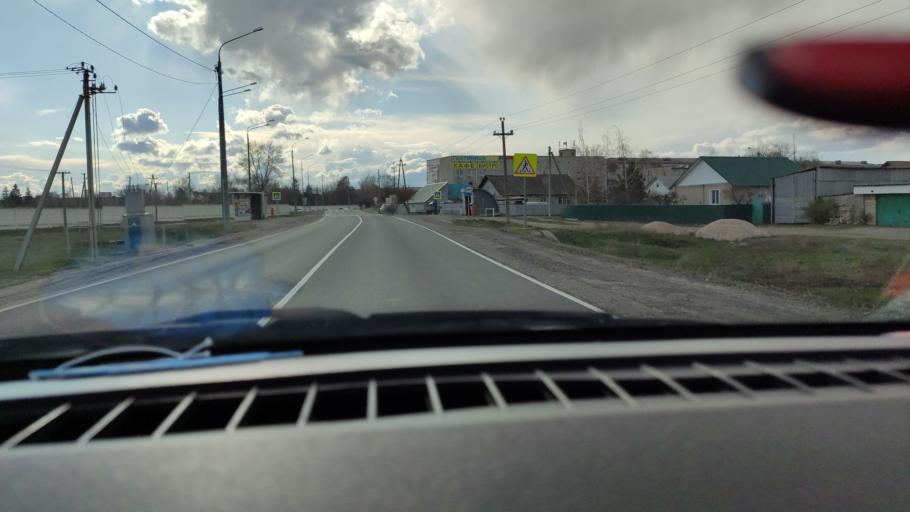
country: RU
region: Saratov
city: Sennoy
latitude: 52.1523
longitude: 46.9590
